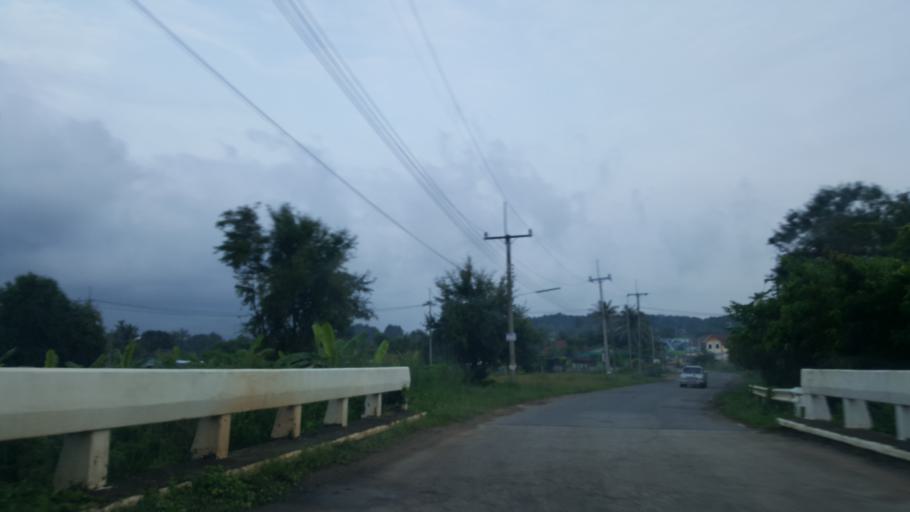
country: TH
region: Chon Buri
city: Sattahip
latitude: 12.7266
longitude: 100.9134
